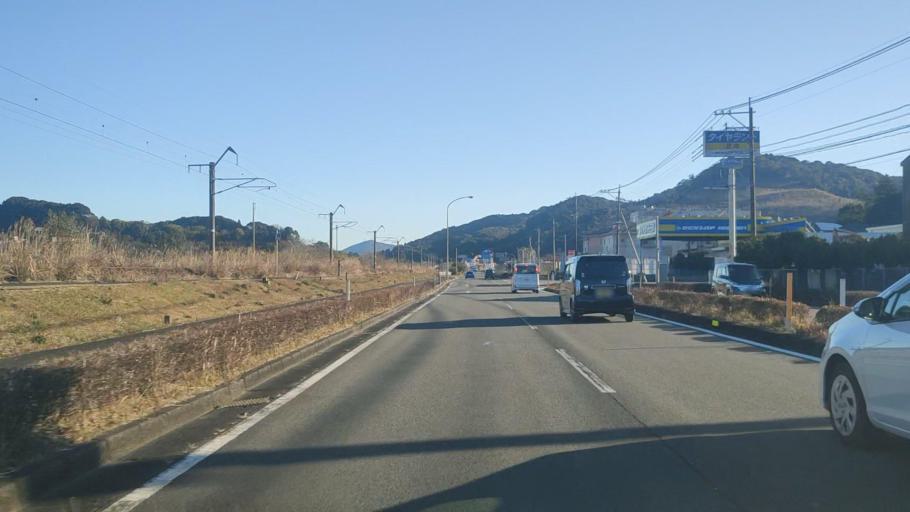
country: JP
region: Miyazaki
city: Nobeoka
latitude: 32.4477
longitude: 131.6343
